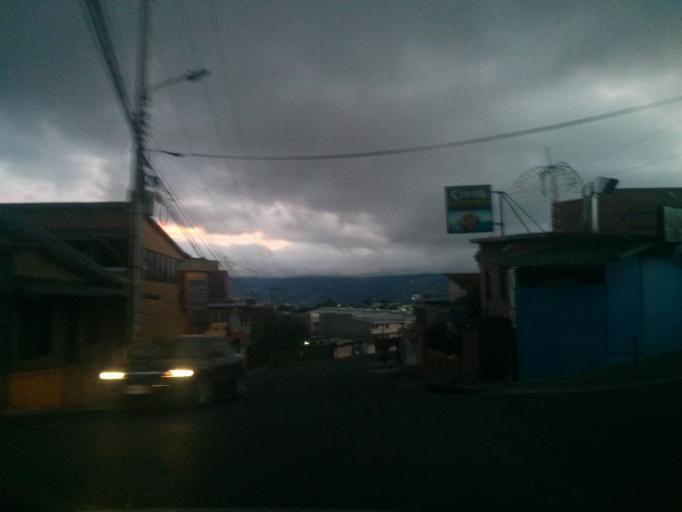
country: CR
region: San Jose
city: Sabanilla
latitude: 9.9372
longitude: -84.0383
